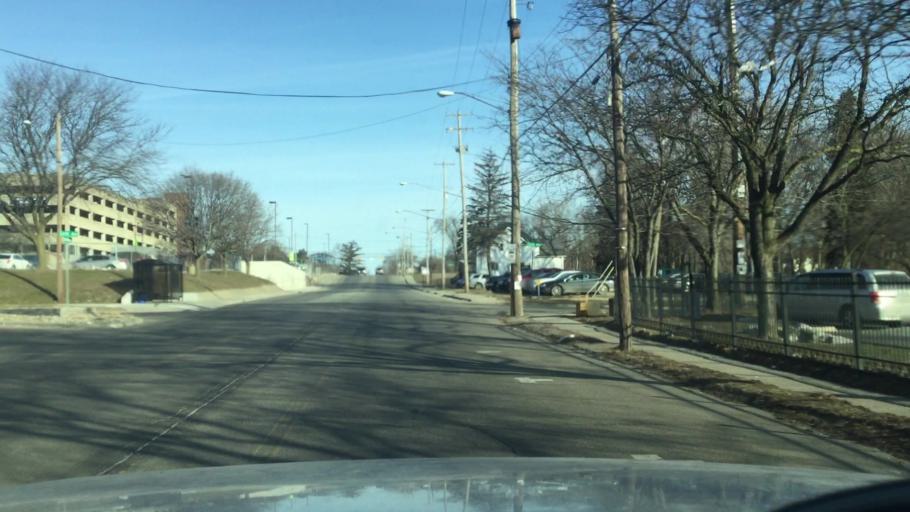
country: US
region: Michigan
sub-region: Genesee County
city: Flint
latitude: 43.0215
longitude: -83.7017
